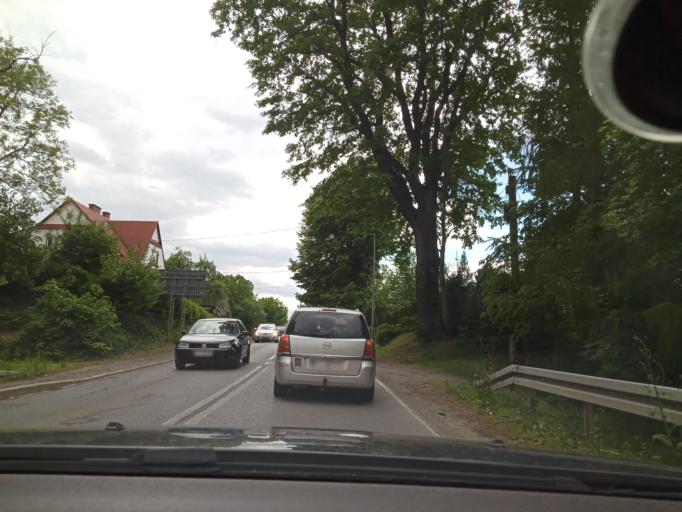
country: PL
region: Lesser Poland Voivodeship
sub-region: Powiat limanowski
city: Limanowa
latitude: 49.7358
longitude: 20.4013
